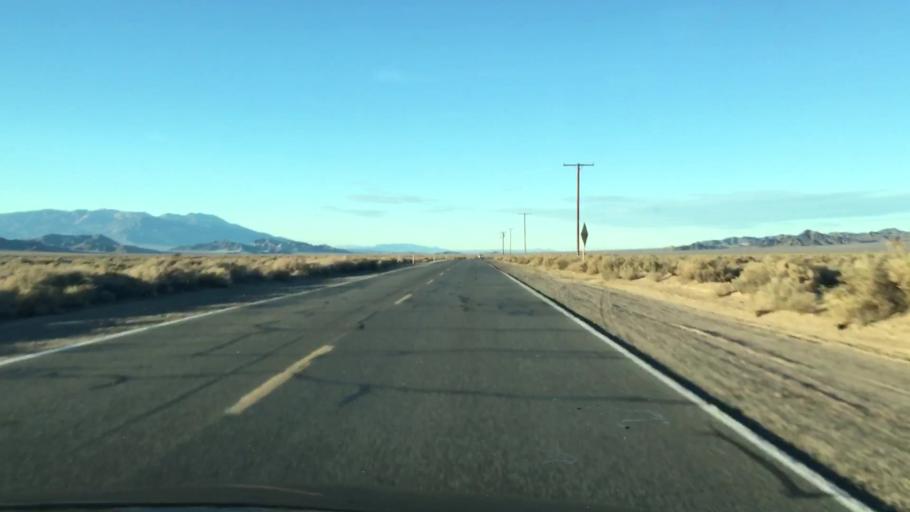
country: US
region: California
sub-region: San Bernardino County
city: Fort Irwin
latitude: 35.2894
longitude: -116.0806
